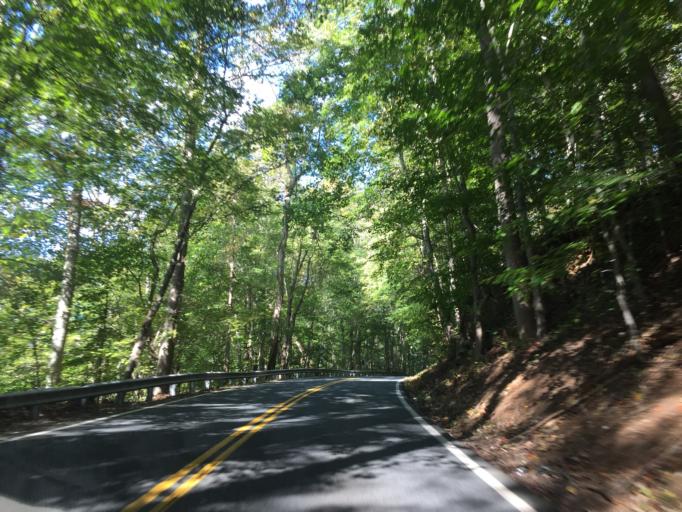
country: US
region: Maryland
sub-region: Harford County
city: Fallston
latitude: 39.5089
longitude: -76.4594
